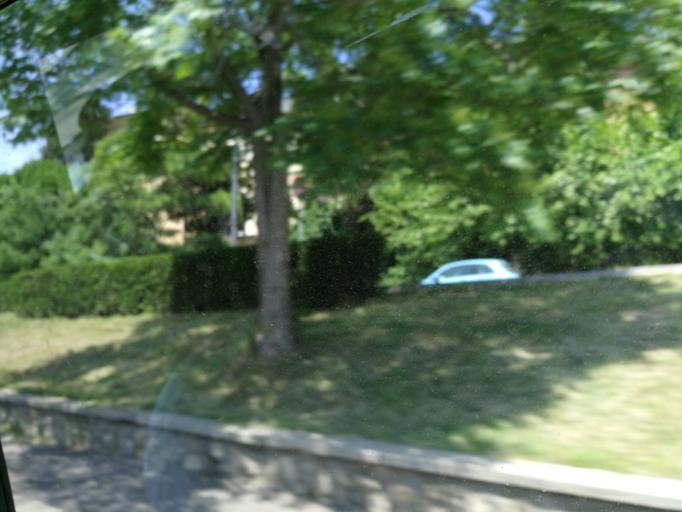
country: RO
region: Constanta
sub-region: Municipiul Constanta
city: Constanta
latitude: 44.1747
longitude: 28.6538
